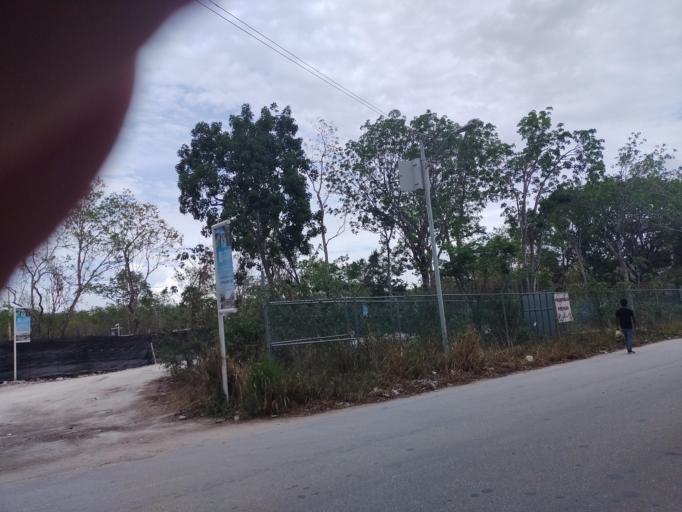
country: MX
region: Quintana Roo
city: Tulum
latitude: 20.2049
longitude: -87.4710
